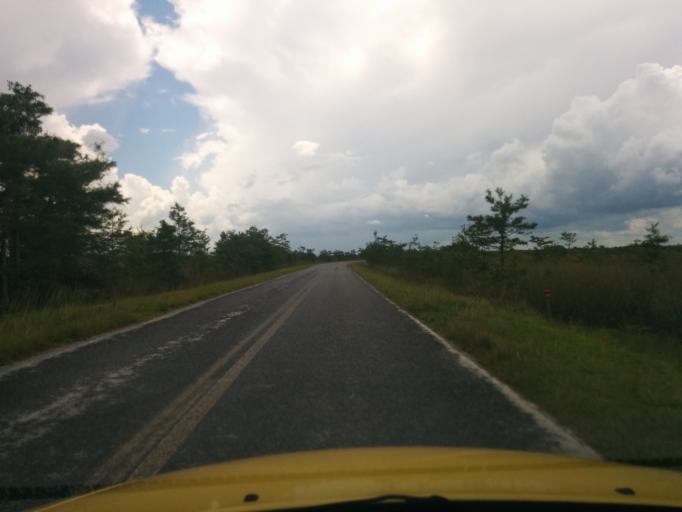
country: US
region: Florida
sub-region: Miami-Dade County
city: Florida City
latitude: 25.4322
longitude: -80.7771
